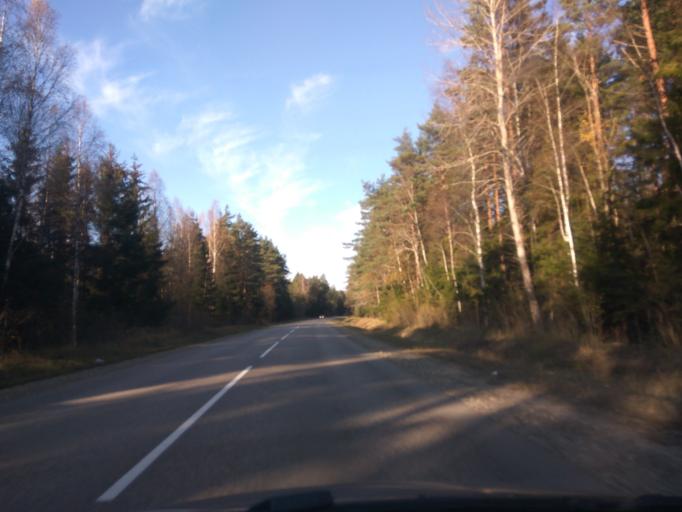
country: LV
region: Ventspils Rajons
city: Piltene
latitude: 57.0811
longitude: 21.7844
